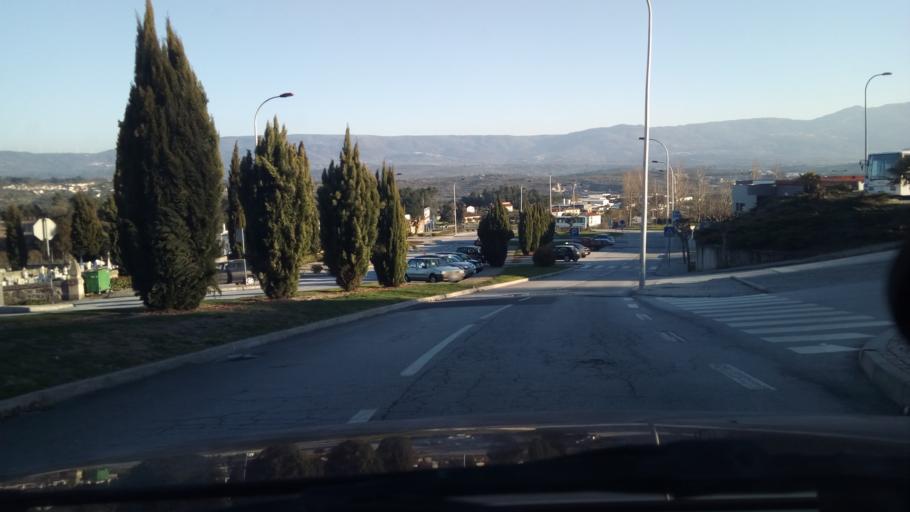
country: PT
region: Guarda
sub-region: Fornos de Algodres
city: Fornos de Algodres
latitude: 40.6201
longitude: -7.5362
